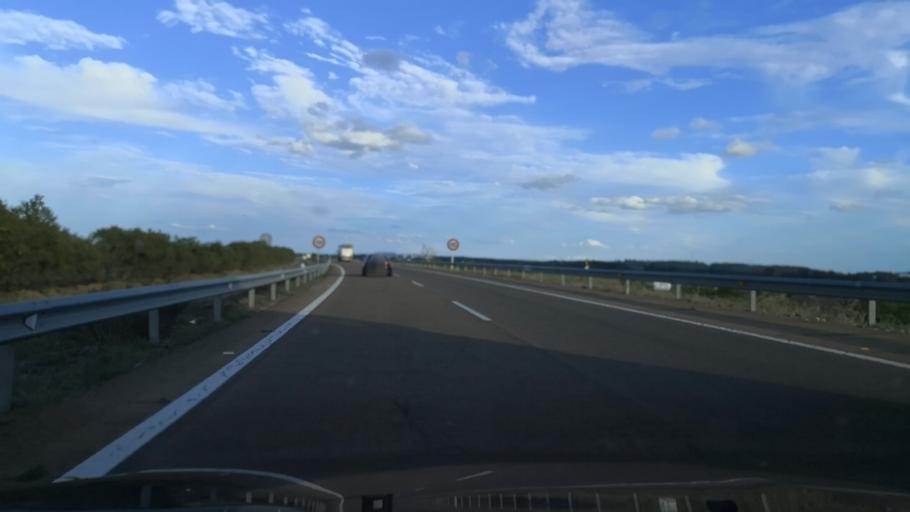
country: ES
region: Extremadura
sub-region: Provincia de Badajoz
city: Badajoz
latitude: 38.9103
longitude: -6.9457
